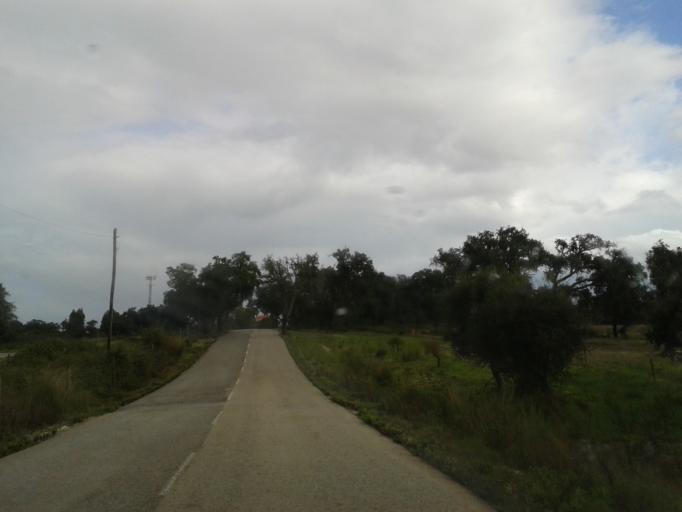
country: PT
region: Santarem
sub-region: Benavente
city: Poceirao
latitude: 38.8356
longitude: -8.7399
